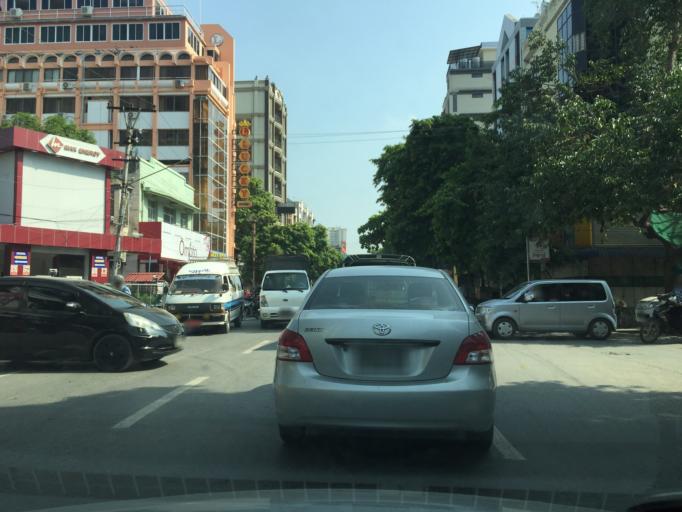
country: MM
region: Mandalay
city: Mandalay
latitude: 21.9742
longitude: 96.0773
